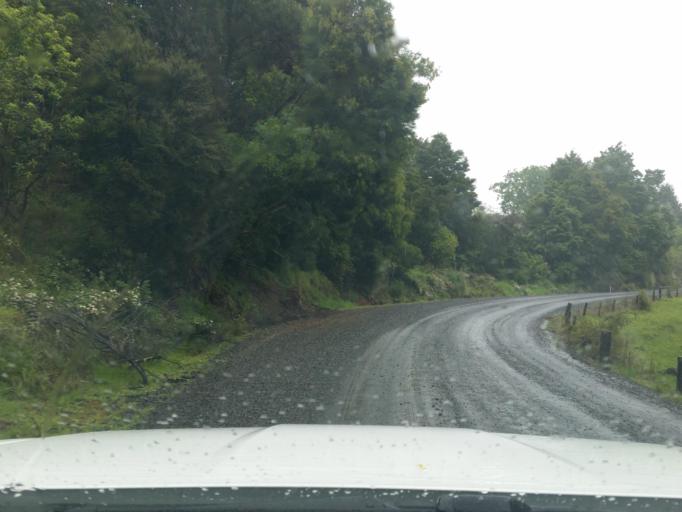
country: NZ
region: Northland
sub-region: Kaipara District
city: Dargaville
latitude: -35.7962
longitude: 173.9801
